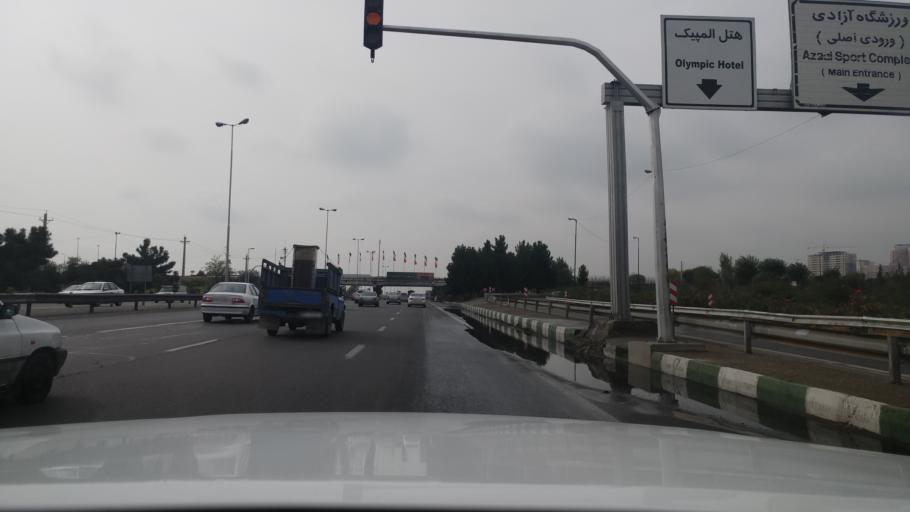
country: IR
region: Tehran
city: Tehran
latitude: 35.7153
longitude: 51.2688
